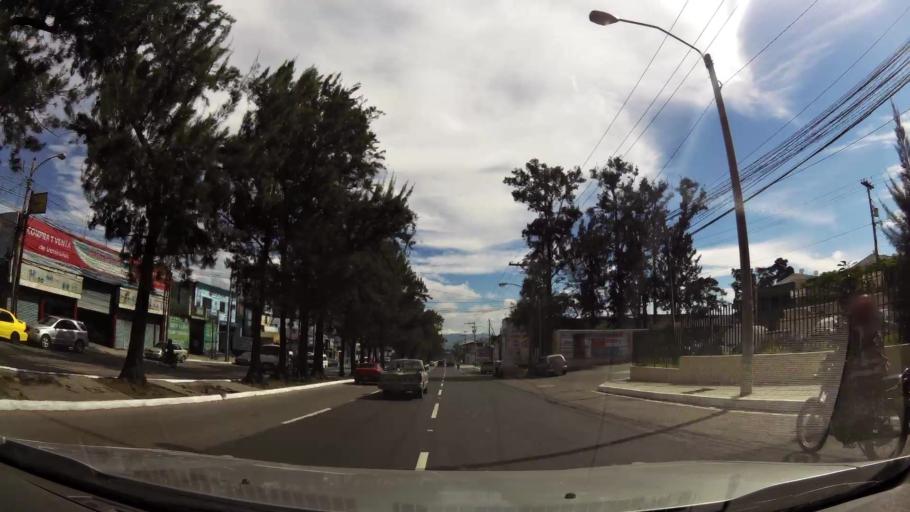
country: GT
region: Guatemala
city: Mixco
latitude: 14.6359
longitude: -90.5618
